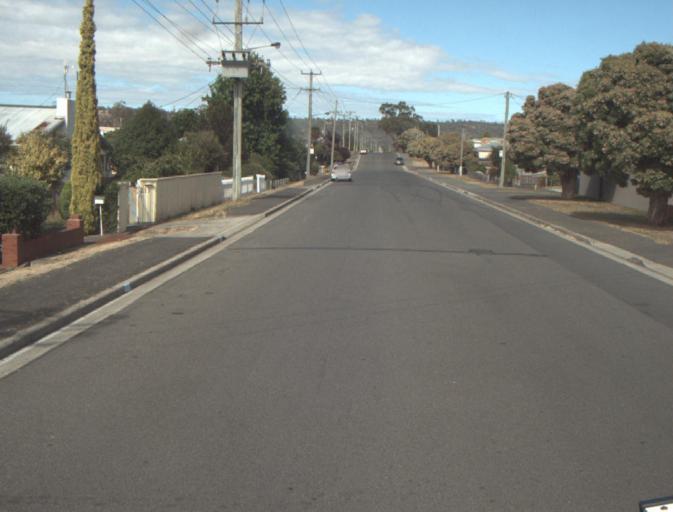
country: AU
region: Tasmania
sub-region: Launceston
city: Summerhill
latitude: -41.4684
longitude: 147.1262
